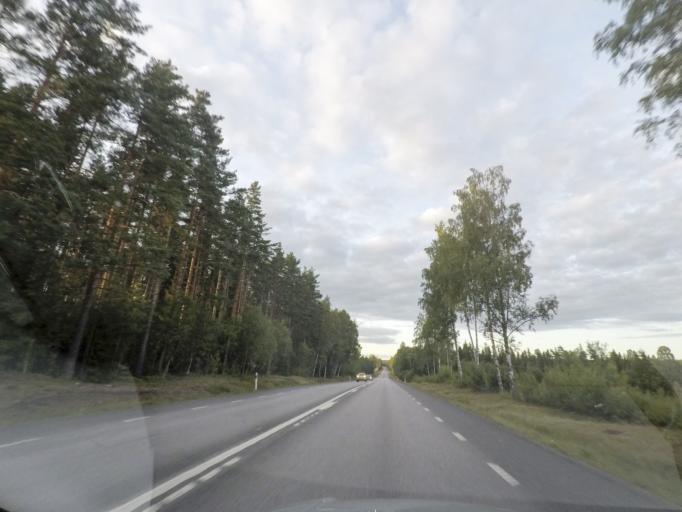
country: SE
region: OErebro
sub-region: Hallefors Kommun
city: Haellefors
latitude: 59.7572
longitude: 14.5133
